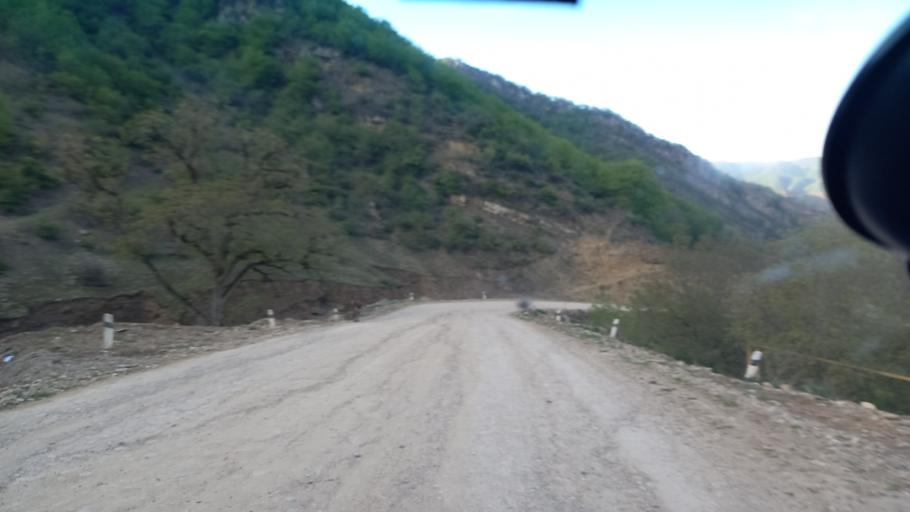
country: RU
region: Dagestan
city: Khuchni
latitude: 41.9677
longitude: 47.8746
